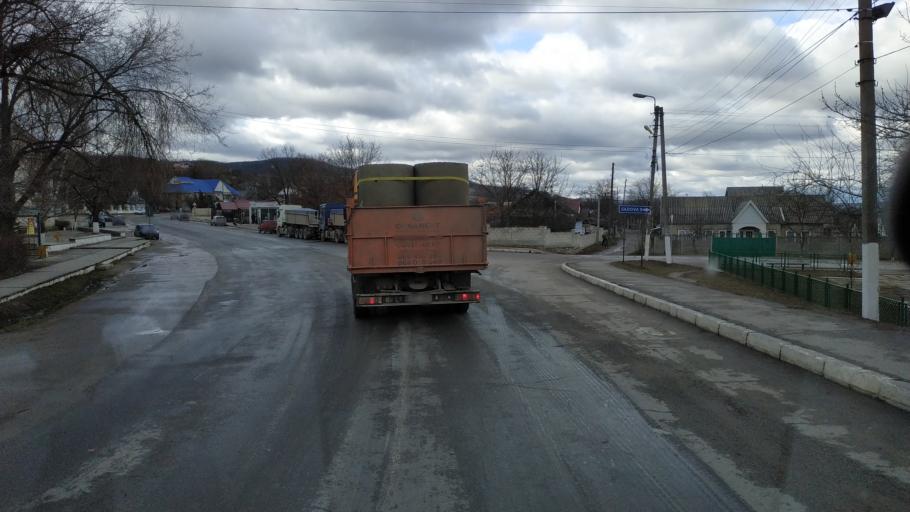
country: MD
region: Stinga Nistrului
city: Bucovat
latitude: 47.1546
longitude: 28.4283
